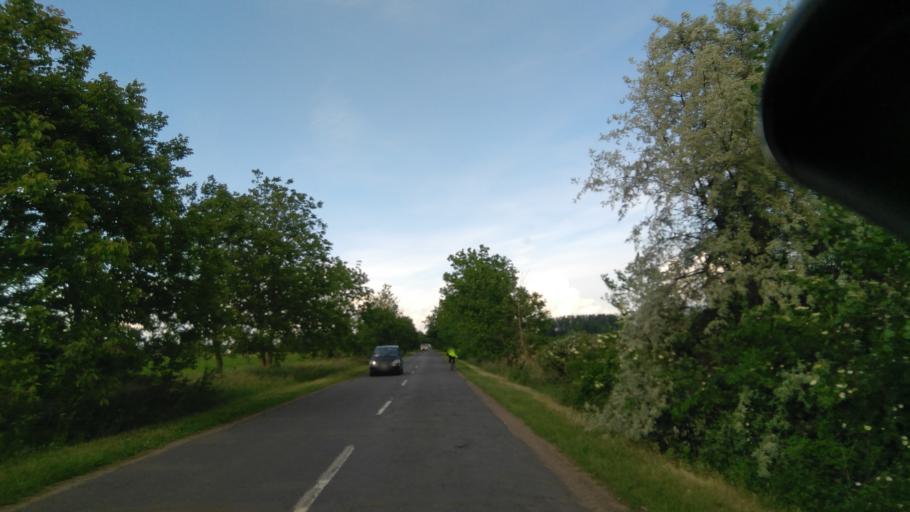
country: HU
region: Bekes
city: Lokoshaza
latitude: 46.4184
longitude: 21.2189
